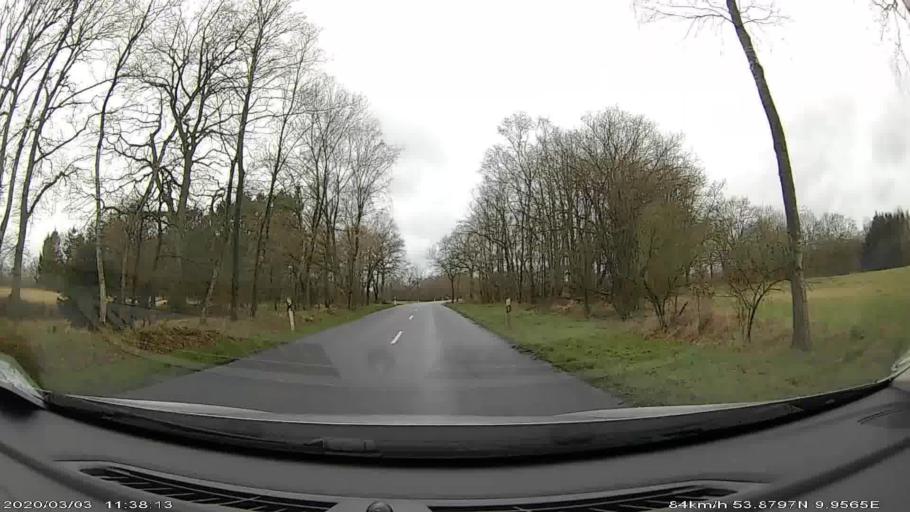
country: DE
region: Schleswig-Holstein
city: Schmalfeld
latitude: 53.8801
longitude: 9.9515
